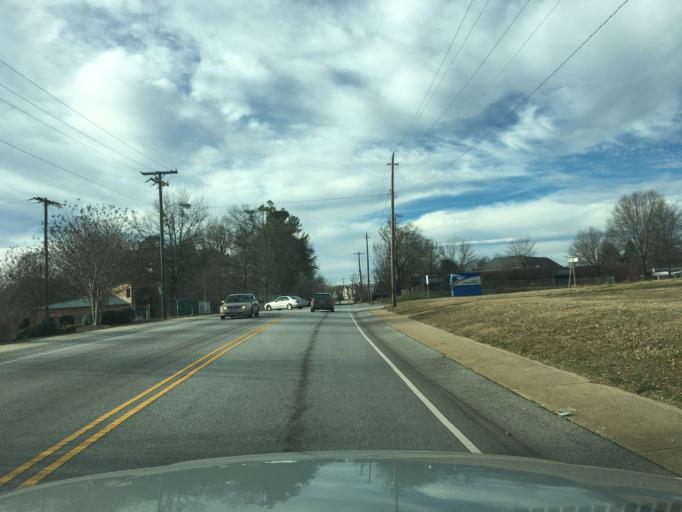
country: US
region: South Carolina
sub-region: Greenville County
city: Greer
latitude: 34.9396
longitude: -82.2464
